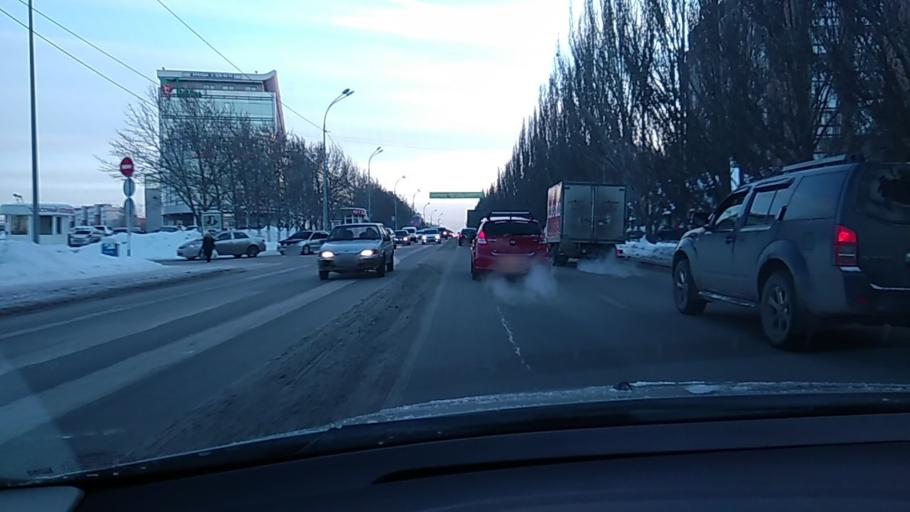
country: RU
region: Sverdlovsk
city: Yekaterinburg
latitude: 56.8351
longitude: 60.6344
